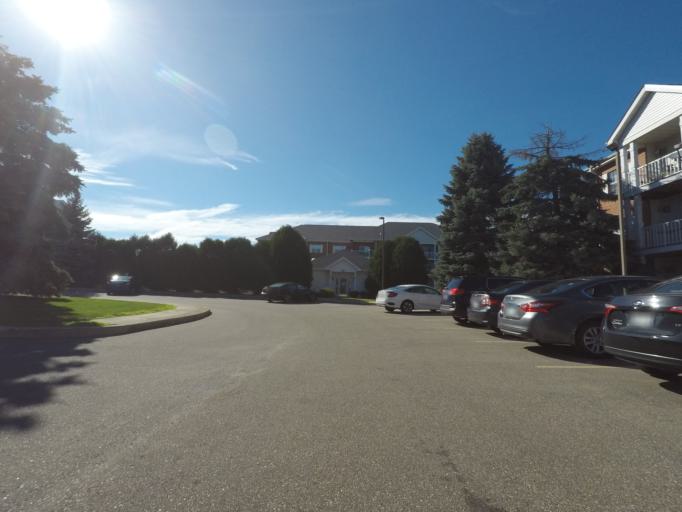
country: US
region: Wisconsin
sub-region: Dane County
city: Middleton
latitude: 43.0657
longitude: -89.5264
